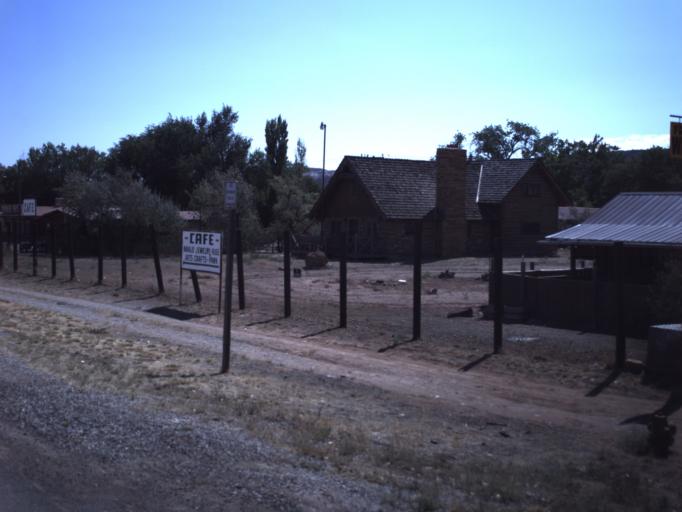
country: US
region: Utah
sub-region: San Juan County
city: Blanding
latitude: 37.2816
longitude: -109.5667
